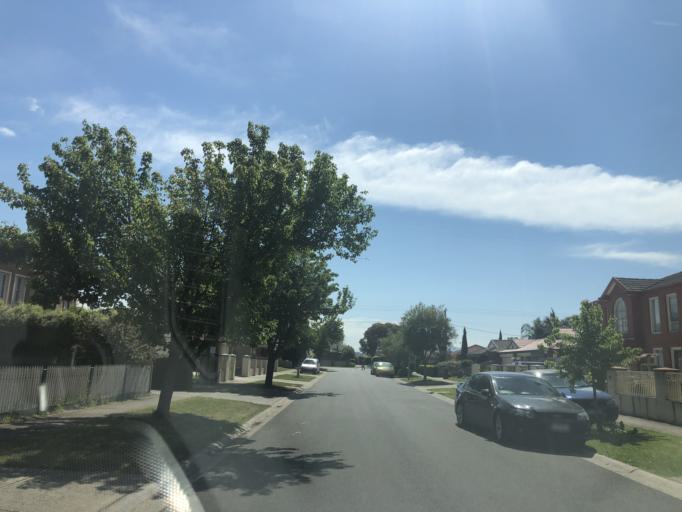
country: AU
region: Victoria
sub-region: Casey
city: Hallam
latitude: -38.0024
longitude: 145.2724
